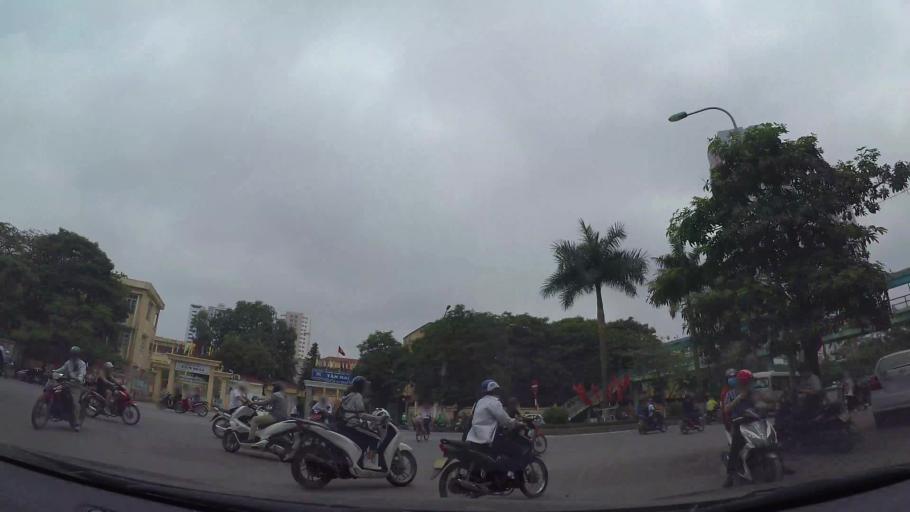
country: VN
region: Ha Noi
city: Hai BaTrung
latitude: 20.9834
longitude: 105.8500
